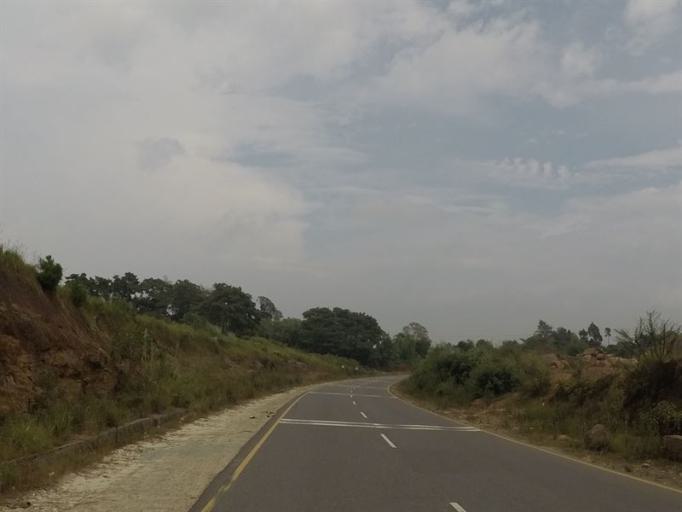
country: IN
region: Meghalaya
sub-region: East Khasi Hills
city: Shillong
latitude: 25.4907
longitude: 92.1822
